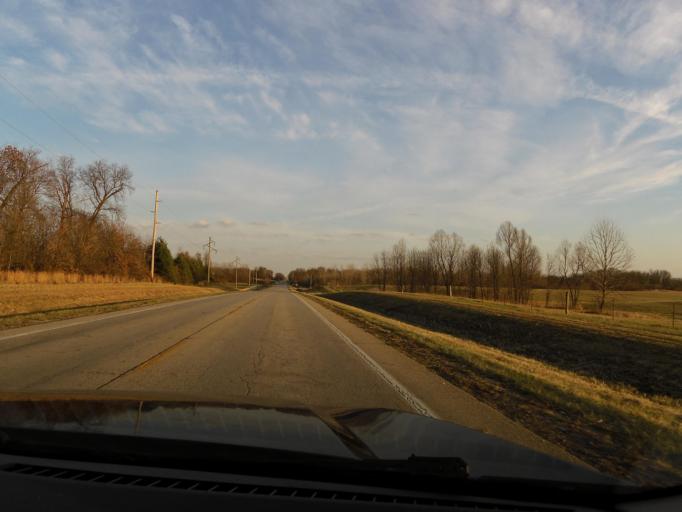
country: US
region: Illinois
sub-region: Fayette County
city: Vandalia
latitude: 38.8931
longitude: -89.0858
